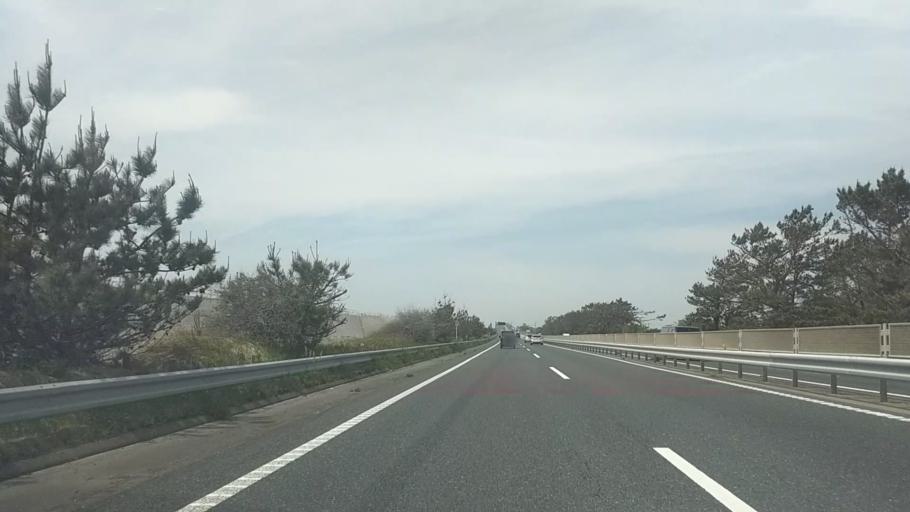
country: JP
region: Shizuoka
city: Kosai-shi
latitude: 34.6781
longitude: 137.6138
